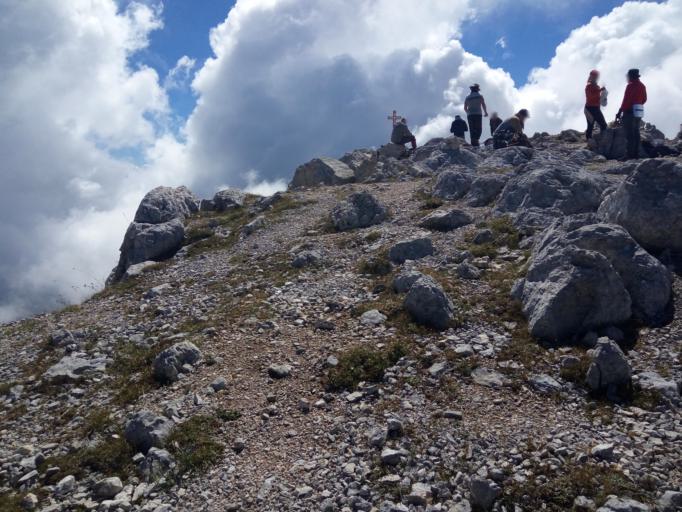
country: RU
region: Adygeya
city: Kamennomostskiy
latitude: 43.9972
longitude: 39.9292
